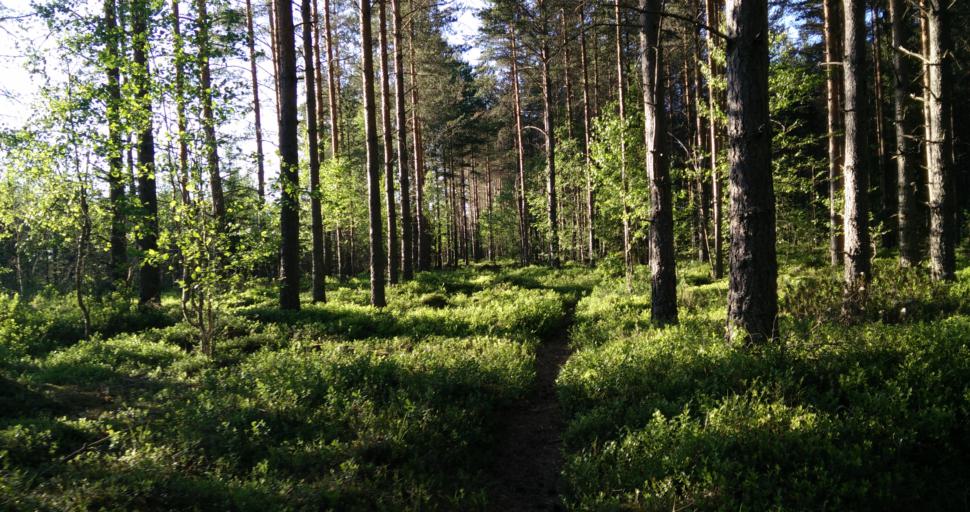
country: SE
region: Vaermland
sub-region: Hagfors Kommun
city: Hagfors
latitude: 60.0193
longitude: 13.5833
